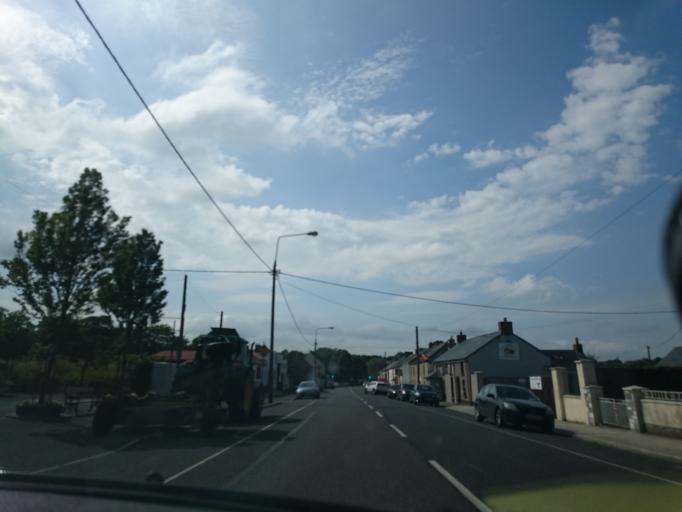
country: IE
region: Leinster
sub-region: Kilkenny
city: Thomastown
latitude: 52.5357
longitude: -7.2265
